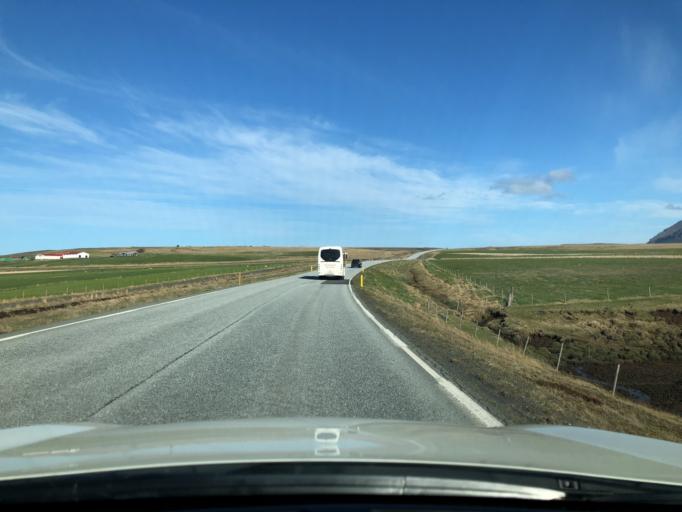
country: IS
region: West
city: Borgarnes
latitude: 64.4021
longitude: -21.9069
